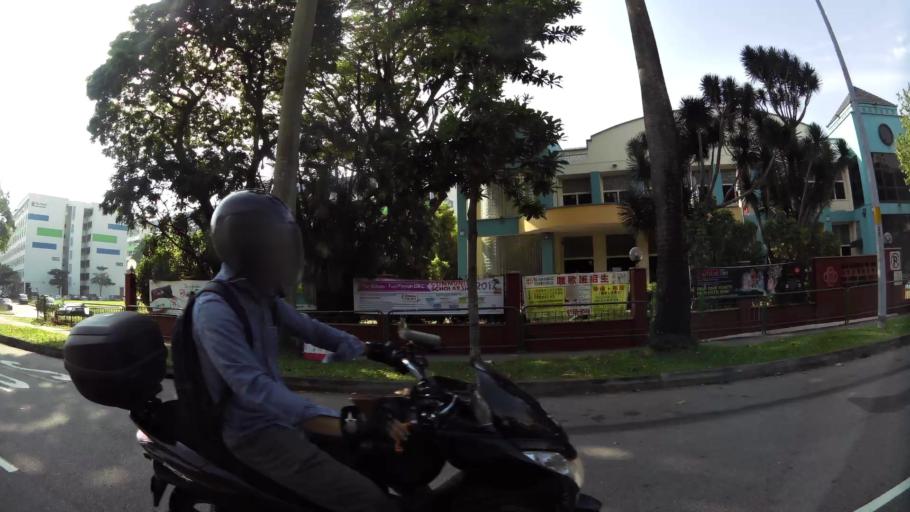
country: SG
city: Singapore
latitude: 1.3353
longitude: 103.8594
